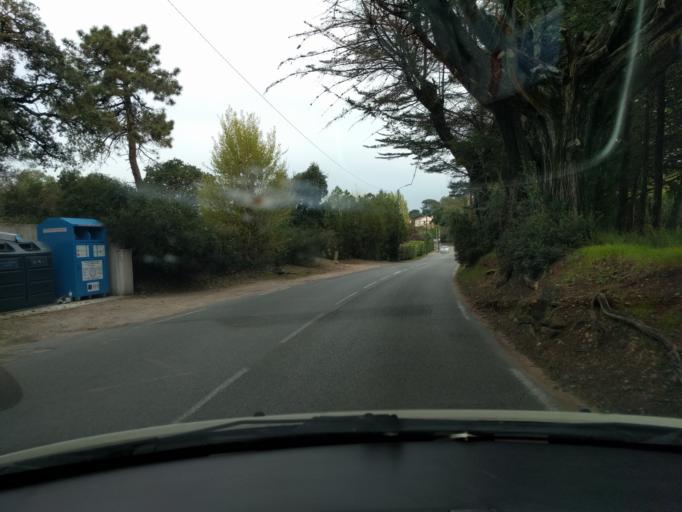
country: FR
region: Provence-Alpes-Cote d'Azur
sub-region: Departement des Alpes-Maritimes
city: La Roquette-sur-Siagne
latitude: 43.5880
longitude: 6.9570
